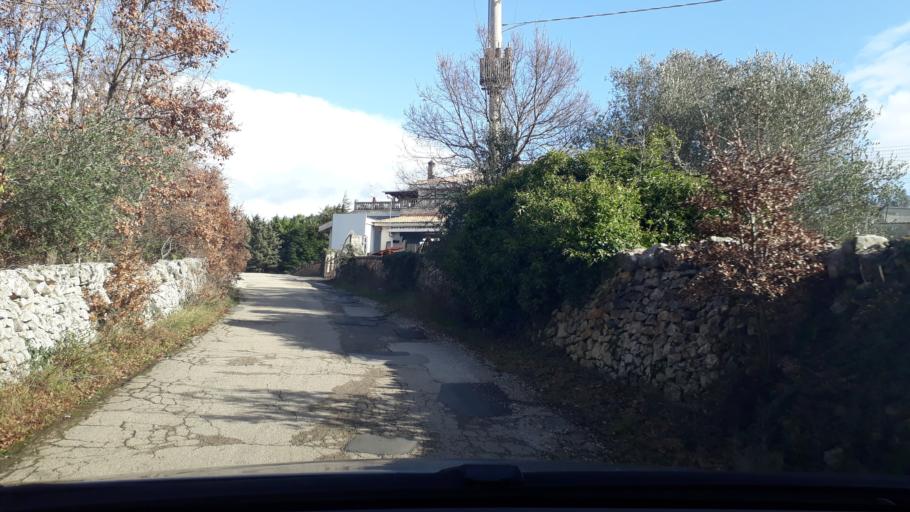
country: IT
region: Apulia
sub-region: Provincia di Brindisi
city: Cisternino
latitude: 40.6925
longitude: 17.4140
